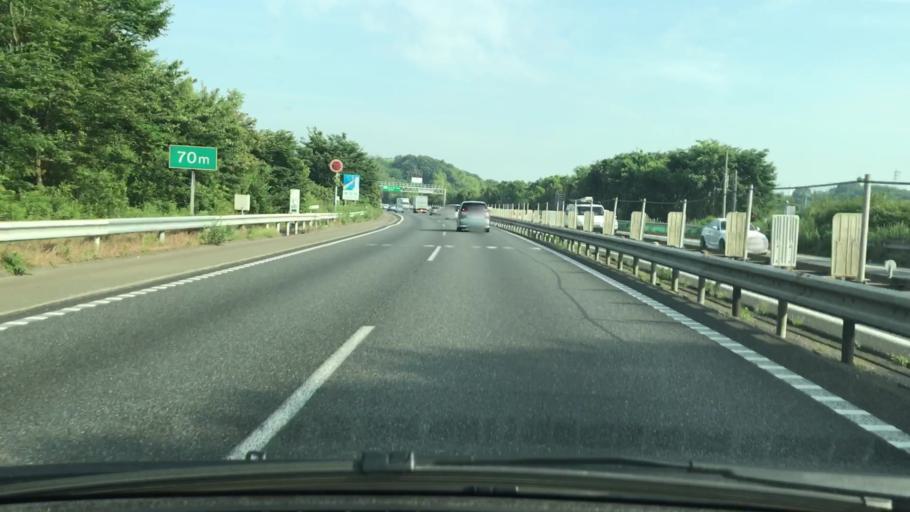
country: JP
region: Hyogo
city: Akashi
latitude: 34.6974
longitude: 134.9672
